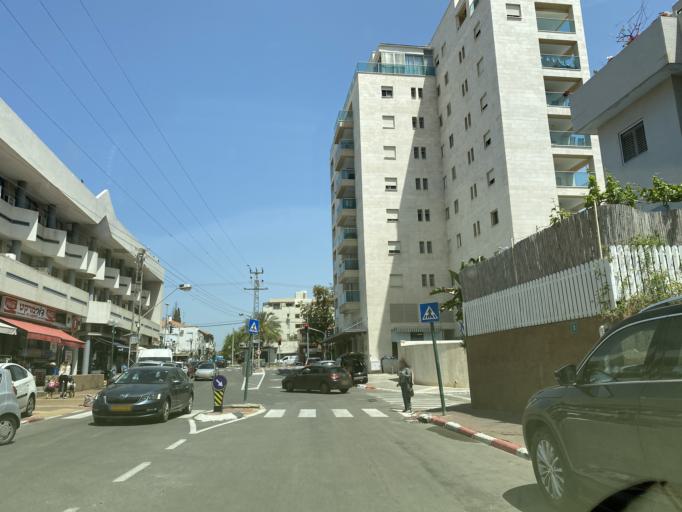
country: IL
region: Central District
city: Ra'anana
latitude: 32.1786
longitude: 34.8794
